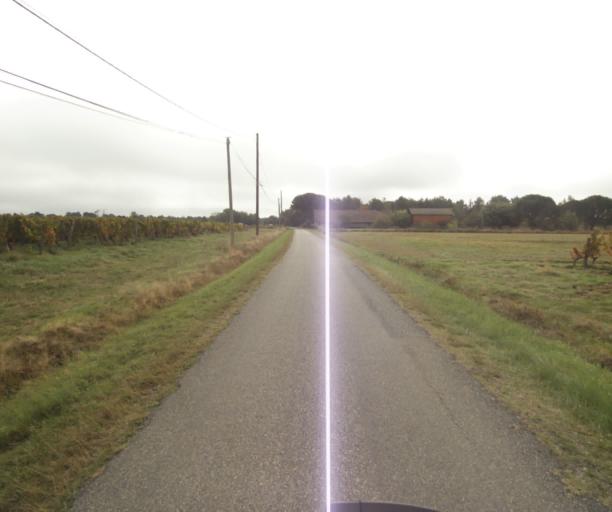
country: FR
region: Midi-Pyrenees
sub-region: Departement du Tarn-et-Garonne
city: Campsas
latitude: 43.8851
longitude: 1.3469
